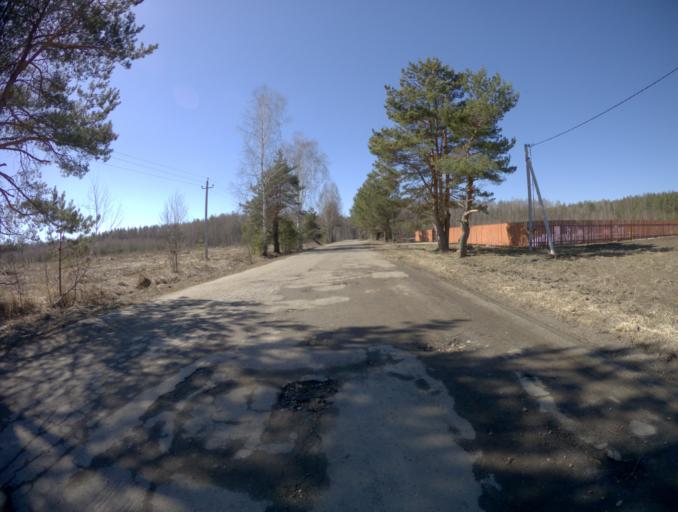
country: RU
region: Vladimir
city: Orgtrud
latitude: 56.2839
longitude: 40.7614
